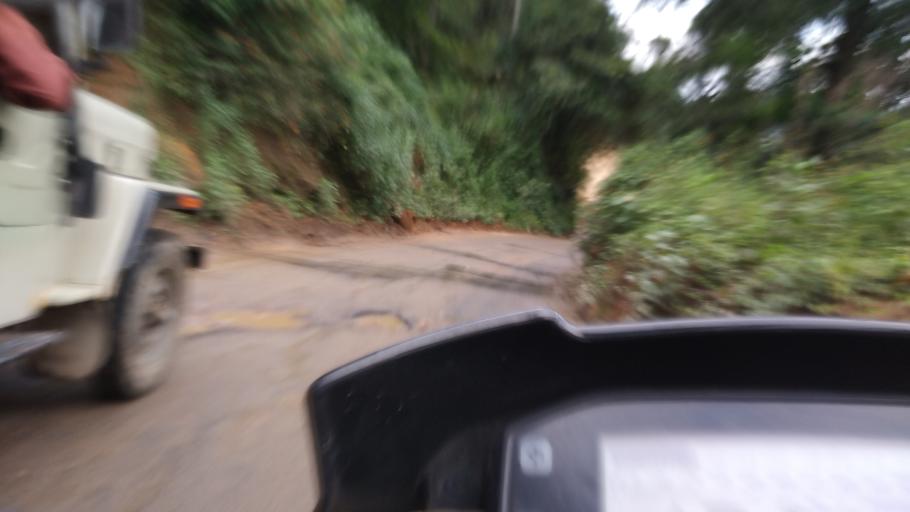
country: IN
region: Tamil Nadu
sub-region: Theni
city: Bodinayakkanur
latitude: 10.0174
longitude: 77.2429
